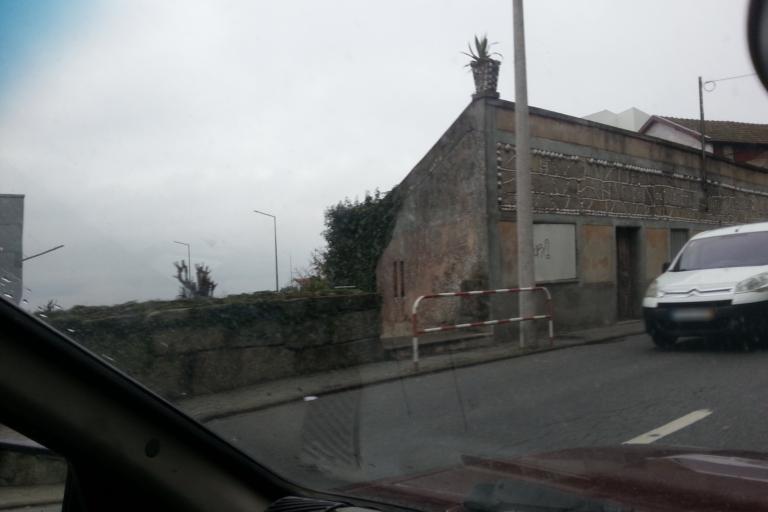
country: PT
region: Viseu
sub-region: Mangualde
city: Mangualde
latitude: 40.6044
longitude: -7.7679
